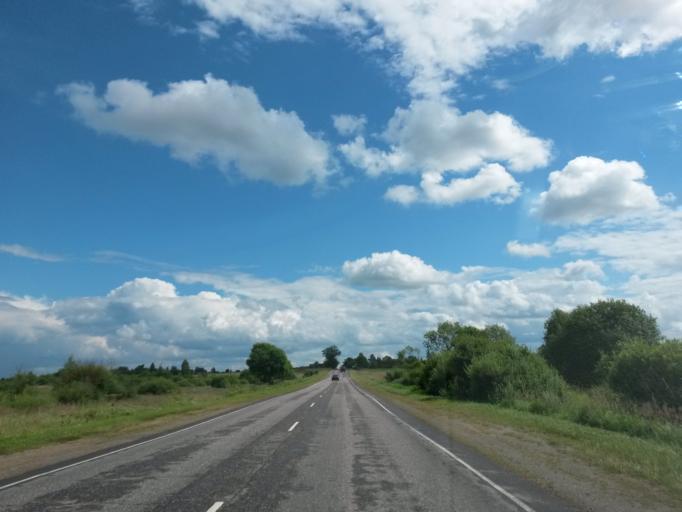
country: RU
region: Ivanovo
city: Pistsovo
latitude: 57.1922
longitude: 40.4106
